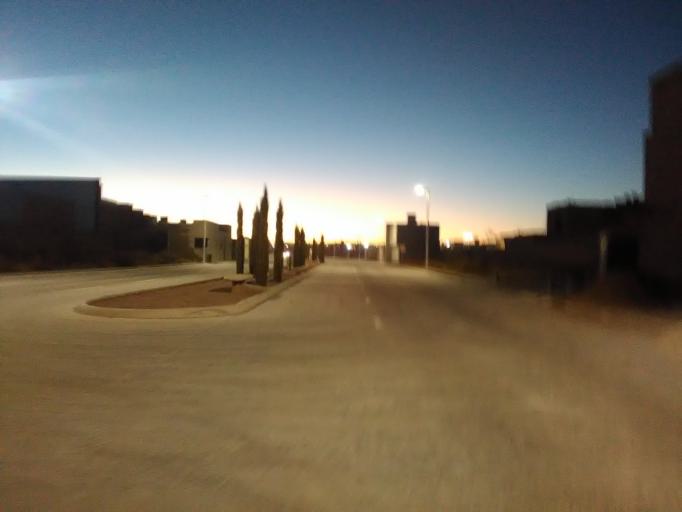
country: MX
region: Durango
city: Victoria de Durango
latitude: 24.0000
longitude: -104.6328
